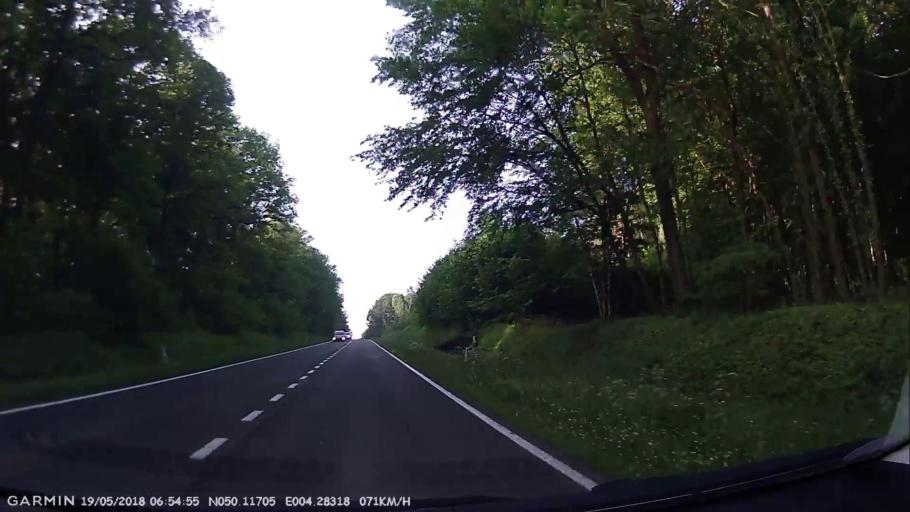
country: BE
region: Wallonia
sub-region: Province du Hainaut
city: Froidchapelle
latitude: 50.1169
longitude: 4.2832
